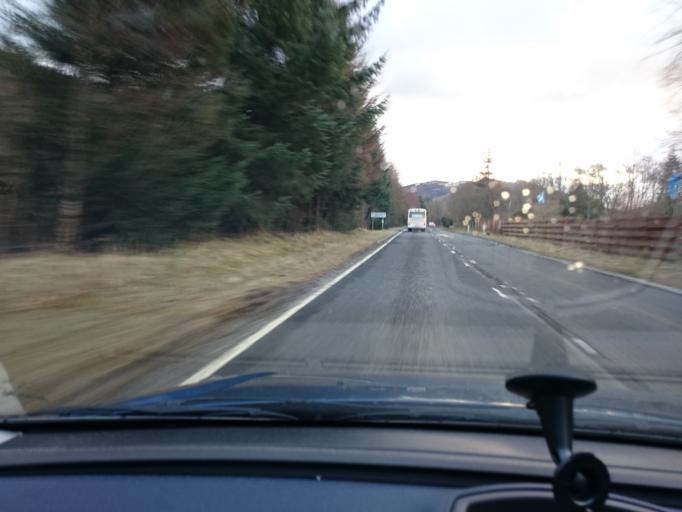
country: GB
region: Scotland
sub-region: Stirling
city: Callander
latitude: 56.3626
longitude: -4.3046
